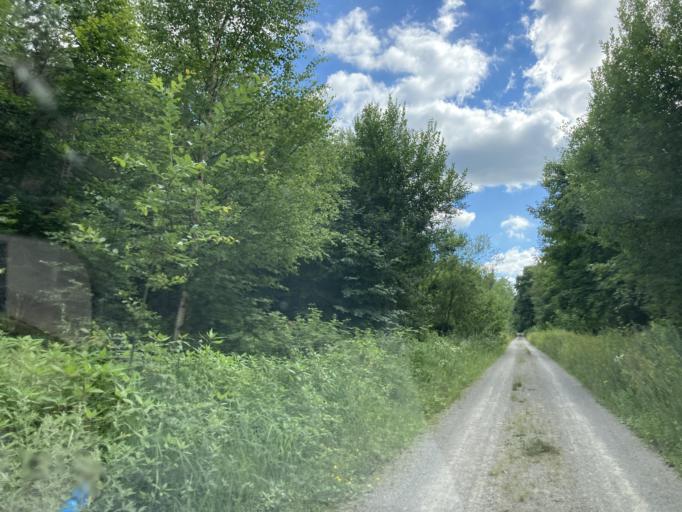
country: DE
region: Baden-Wuerttemberg
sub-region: Tuebingen Region
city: Ofterdingen
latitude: 48.4409
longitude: 9.0110
